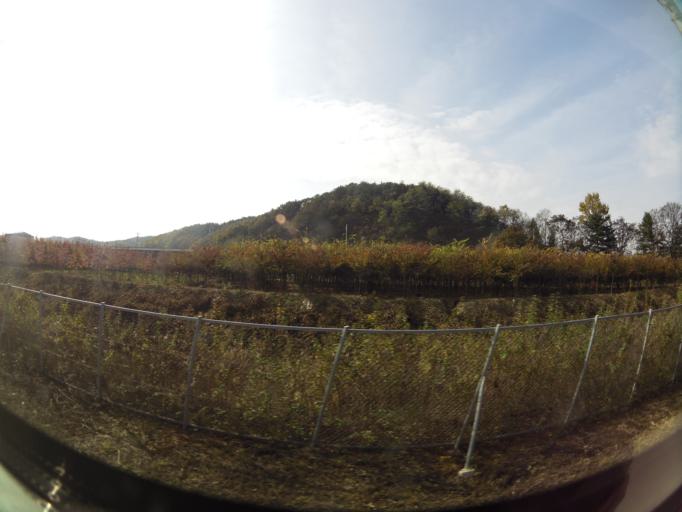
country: KR
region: Chungcheongbuk-do
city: Cheongju-si
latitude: 36.6337
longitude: 127.2887
